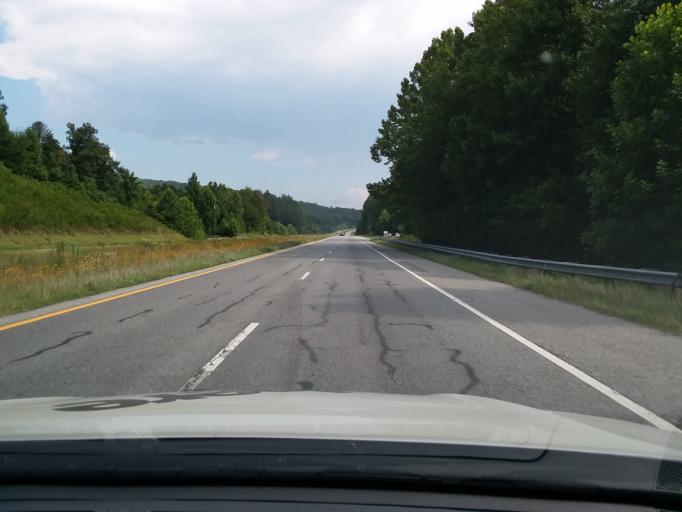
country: US
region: Georgia
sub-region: Rabun County
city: Clayton
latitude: 34.7663
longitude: -83.3974
